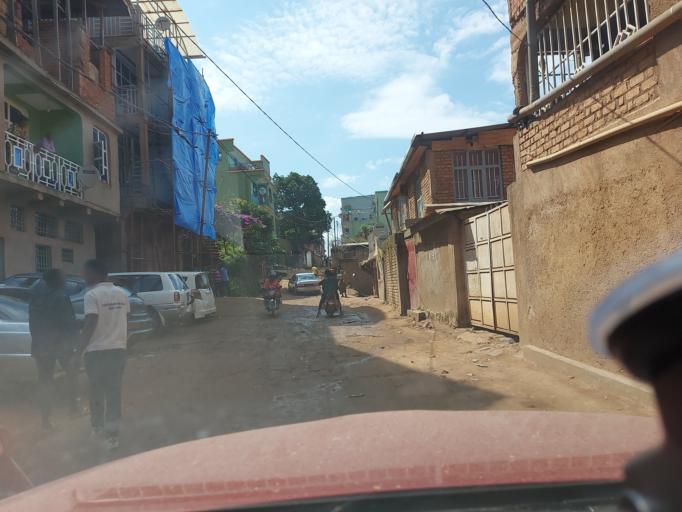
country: CD
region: South Kivu
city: Bukavu
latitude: -2.5014
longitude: 28.8747
